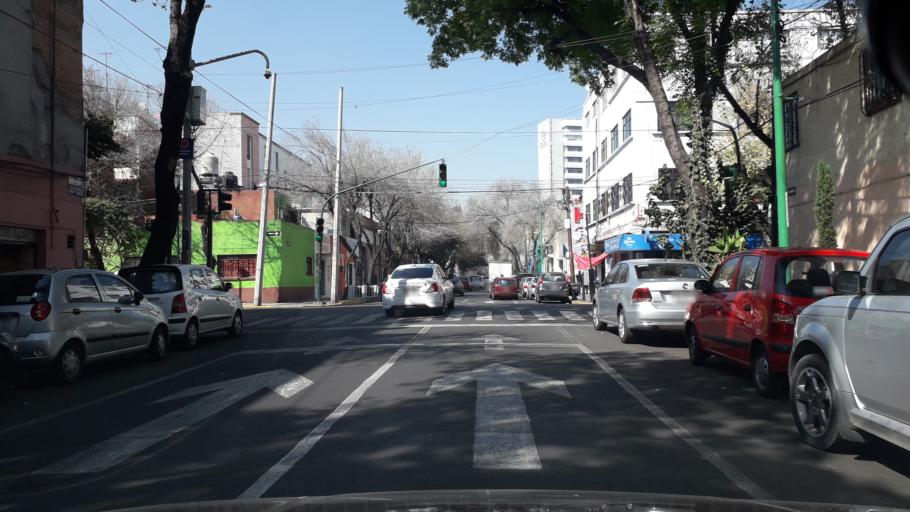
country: MX
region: Mexico City
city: Cuauhtemoc
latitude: 19.4436
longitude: -99.1491
